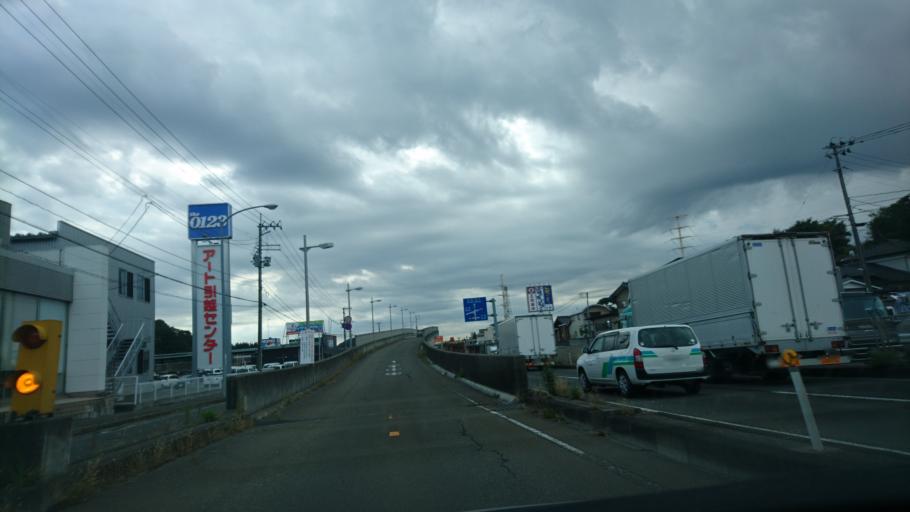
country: JP
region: Miyagi
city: Tomiya
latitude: 38.3394
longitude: 140.8847
